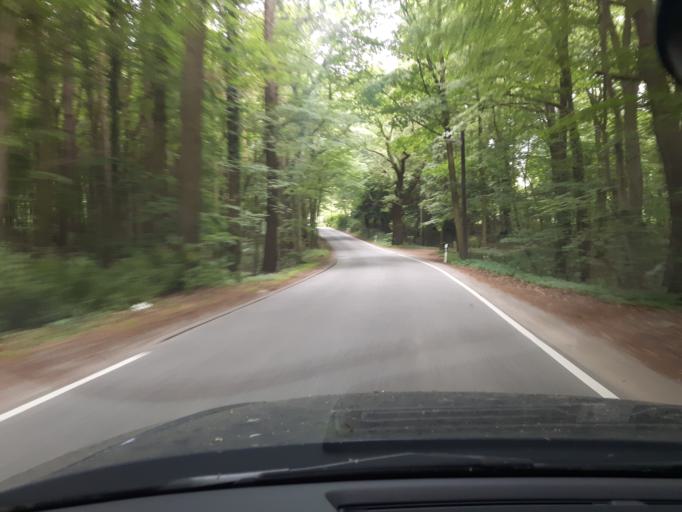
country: DE
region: Schleswig-Holstein
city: Ratekau
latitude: 53.9163
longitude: 10.7920
